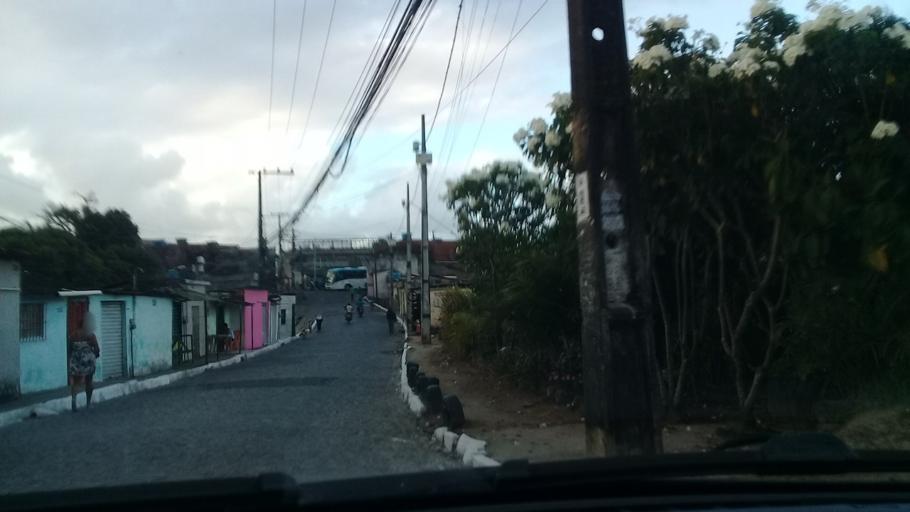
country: BR
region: Pernambuco
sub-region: Jaboatao Dos Guararapes
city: Jaboatao dos Guararapes
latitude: -8.1234
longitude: -34.9539
